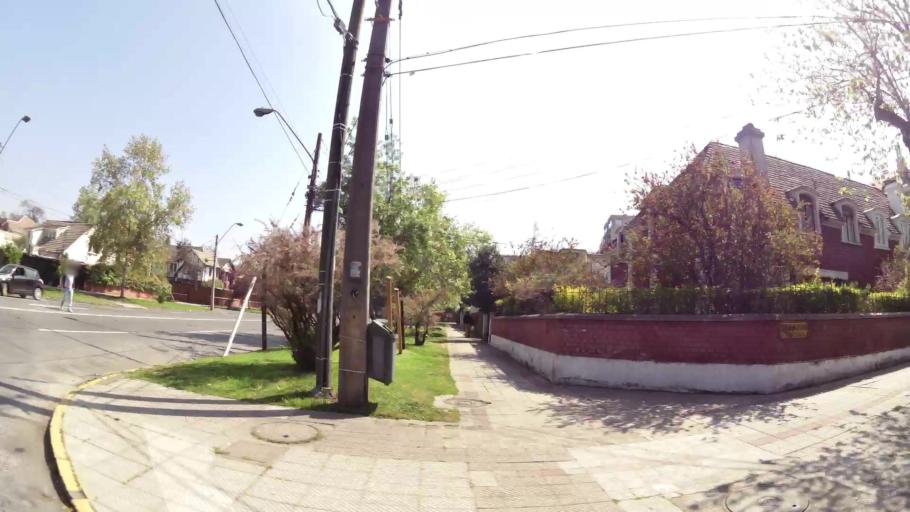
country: CL
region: Santiago Metropolitan
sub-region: Provincia de Santiago
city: Villa Presidente Frei, Nunoa, Santiago, Chile
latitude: -33.4380
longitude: -70.5915
